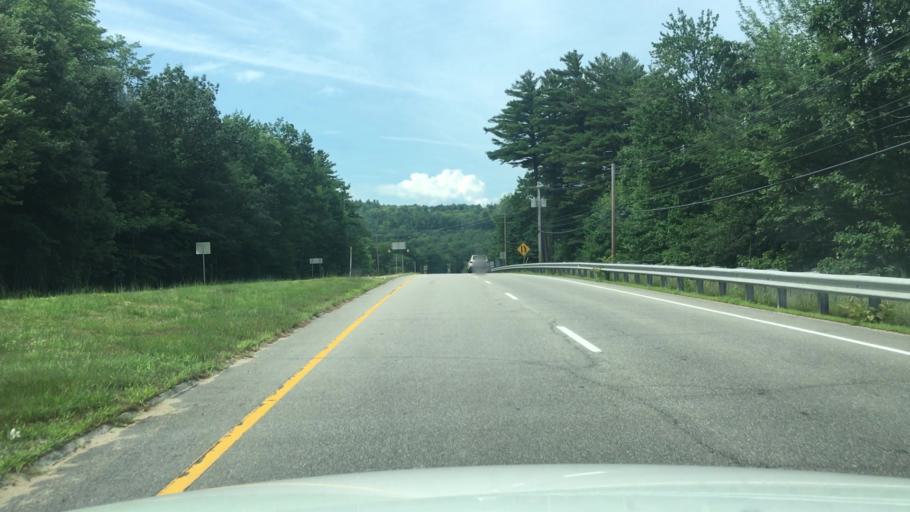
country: US
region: New Hampshire
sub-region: Belknap County
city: Meredith
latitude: 43.6454
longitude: -71.5025
